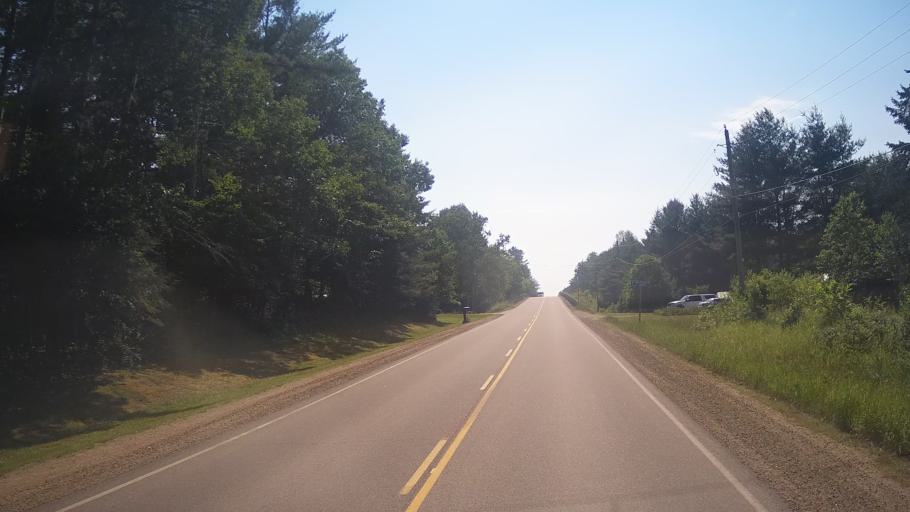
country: CA
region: Ontario
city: Pembroke
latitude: 45.6176
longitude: -77.1758
